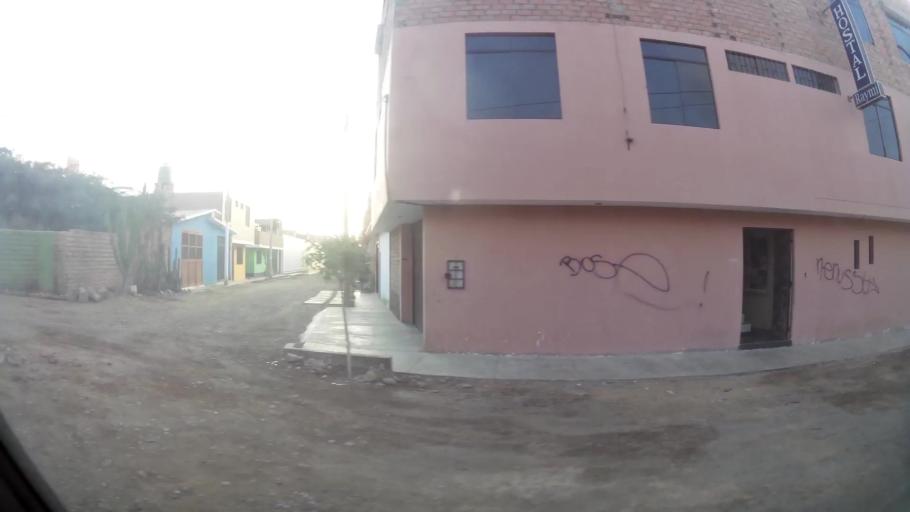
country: PE
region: Lima
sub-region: Huaura
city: Huacho
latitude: -11.1085
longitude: -77.5980
